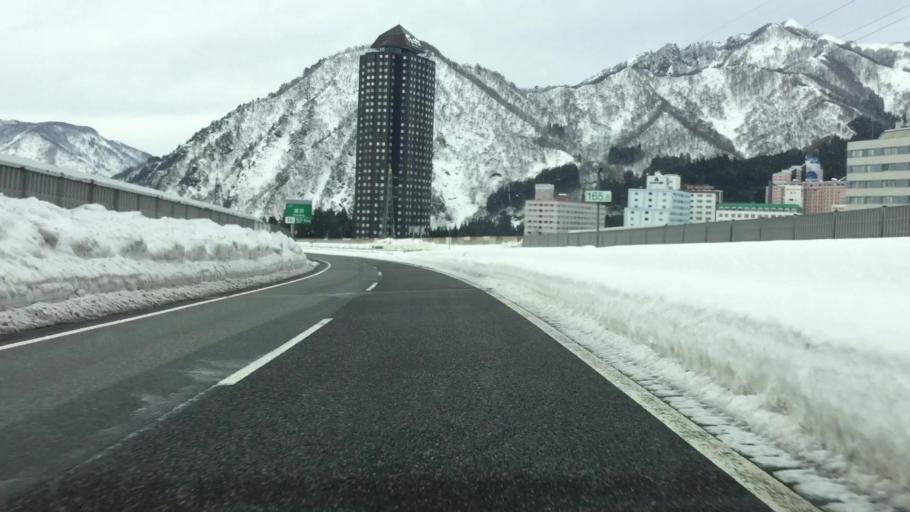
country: JP
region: Niigata
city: Shiozawa
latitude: 36.9270
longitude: 138.8403
